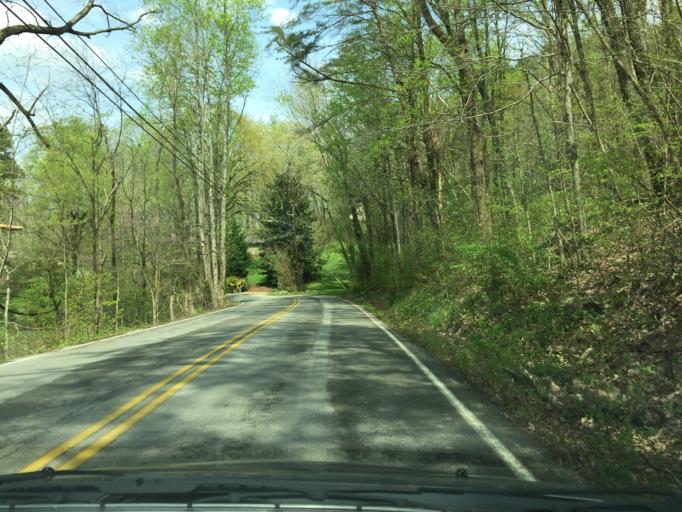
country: US
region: Tennessee
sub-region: Hamilton County
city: Walden
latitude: 35.1484
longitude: -85.2850
